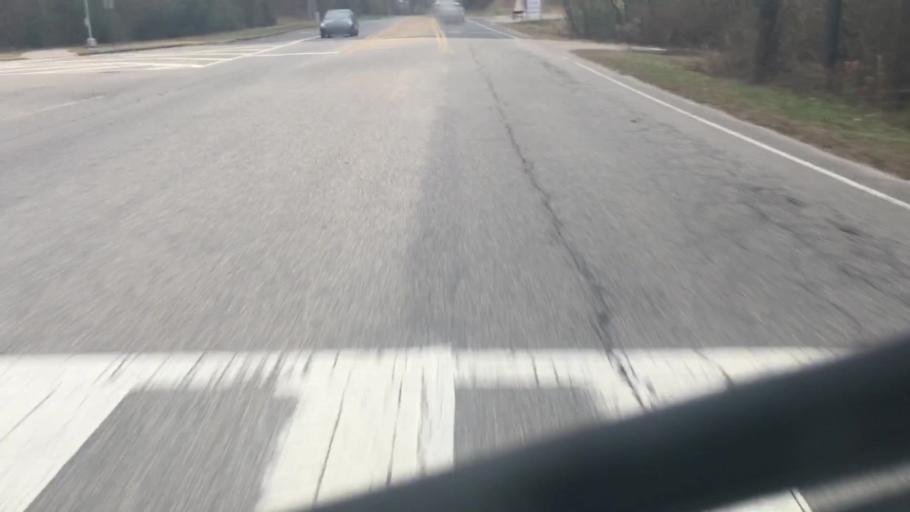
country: US
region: Alabama
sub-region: Jefferson County
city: Hoover
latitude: 33.3588
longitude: -86.8104
